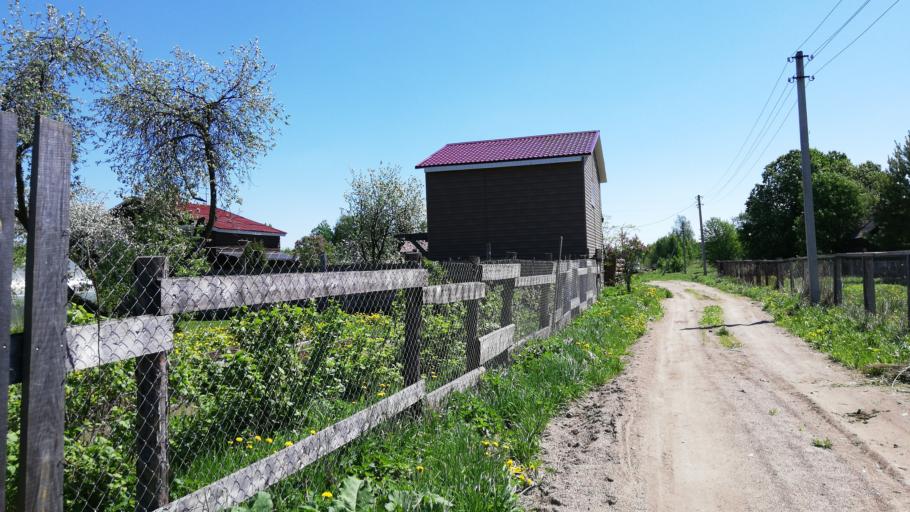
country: RU
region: Ivanovo
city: Pistsovo
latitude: 57.1166
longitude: 40.5956
